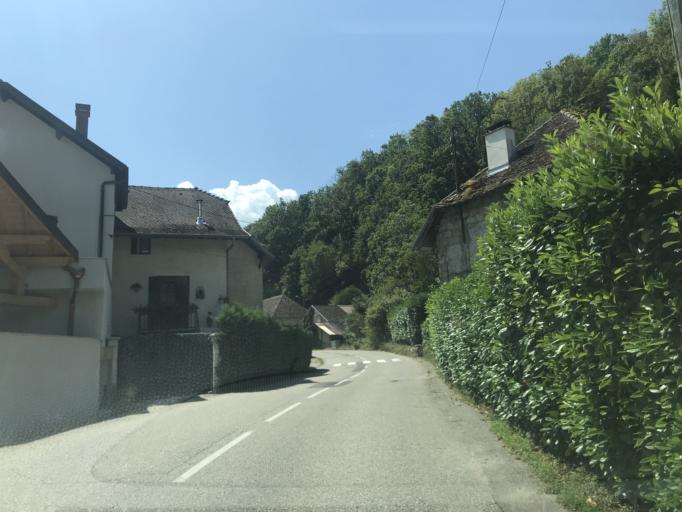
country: FR
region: Rhone-Alpes
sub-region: Departement de la Savoie
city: Chatillon
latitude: 45.8065
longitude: 5.8174
